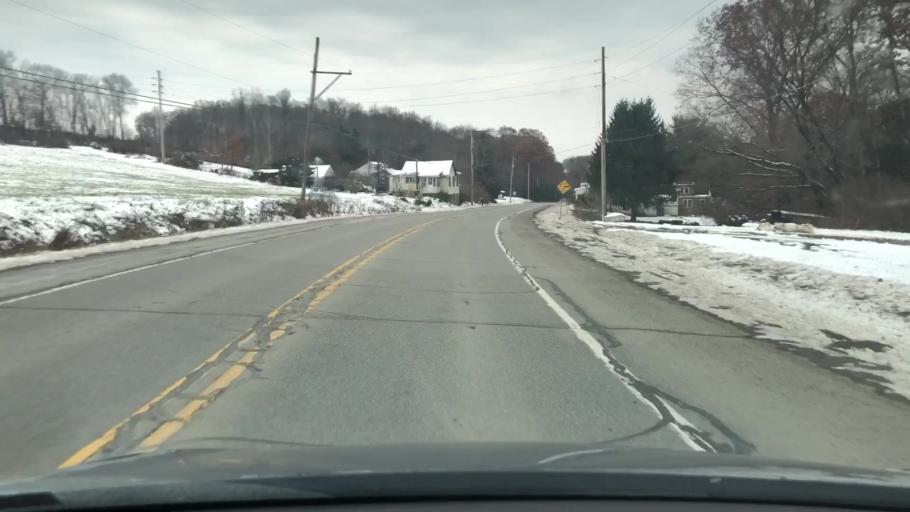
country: US
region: Pennsylvania
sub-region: Jefferson County
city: Brookville
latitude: 41.1534
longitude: -79.1004
